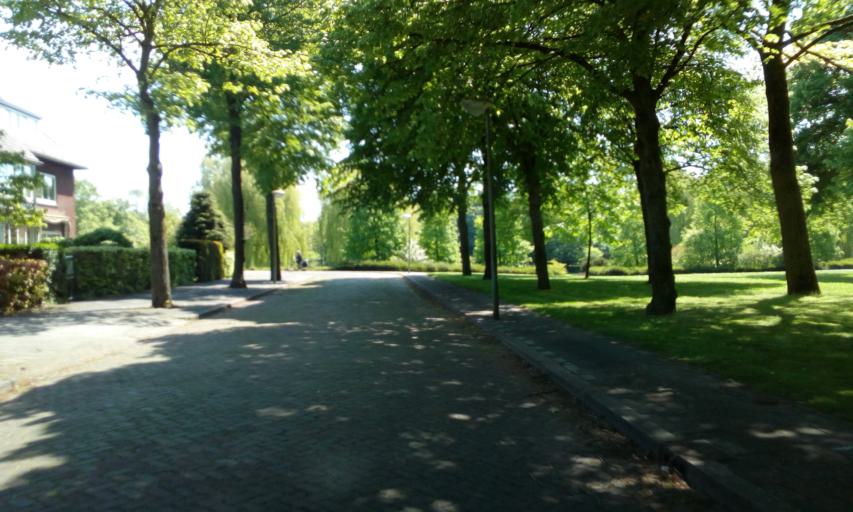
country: NL
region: South Holland
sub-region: Gemeente Papendrecht
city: Papendrecht
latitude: 51.8152
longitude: 4.6898
